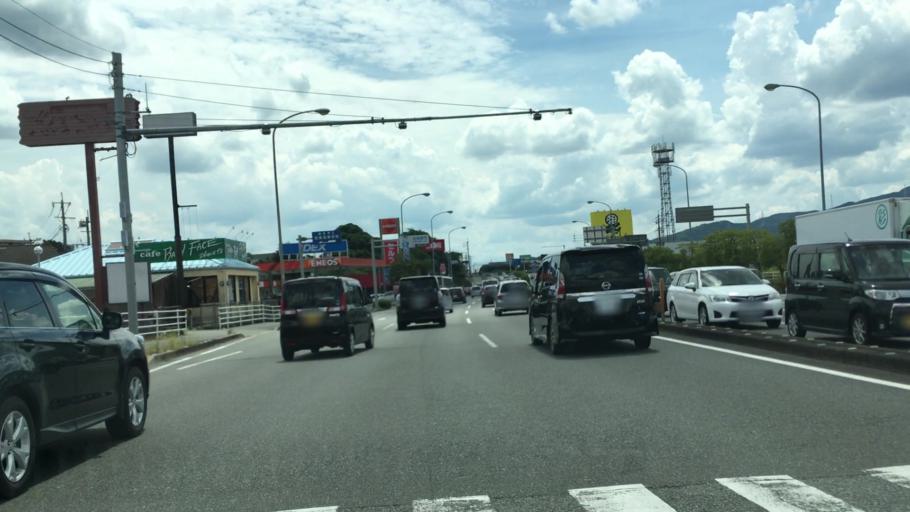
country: JP
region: Fukuoka
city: Chikushino-shi
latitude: 33.4943
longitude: 130.5355
